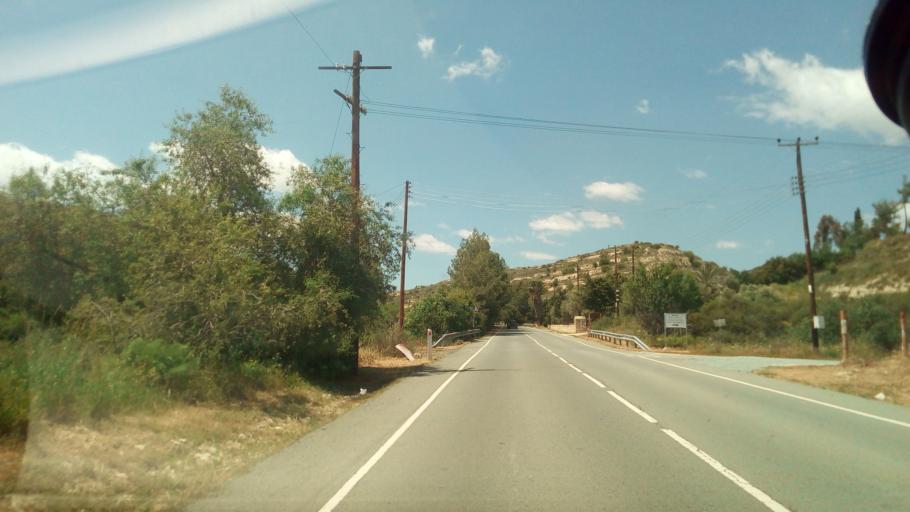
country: CY
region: Limassol
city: Pachna
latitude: 34.7950
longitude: 32.8182
